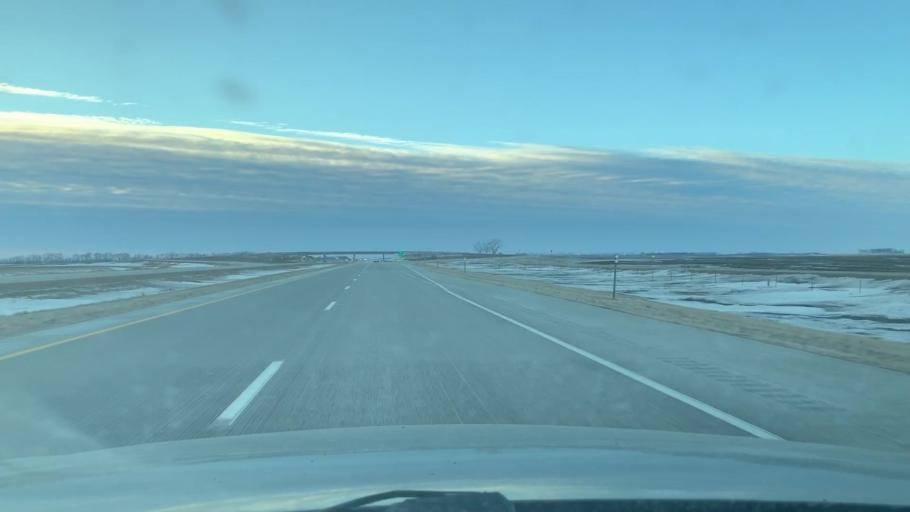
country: US
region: North Dakota
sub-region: Cass County
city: Casselton
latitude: 46.8758
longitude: -97.4858
